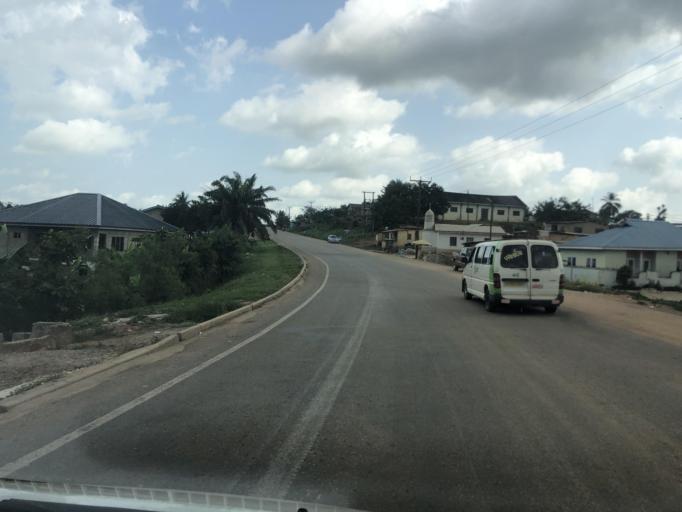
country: GH
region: Central
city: Elmina
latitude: 5.2370
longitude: -1.3316
